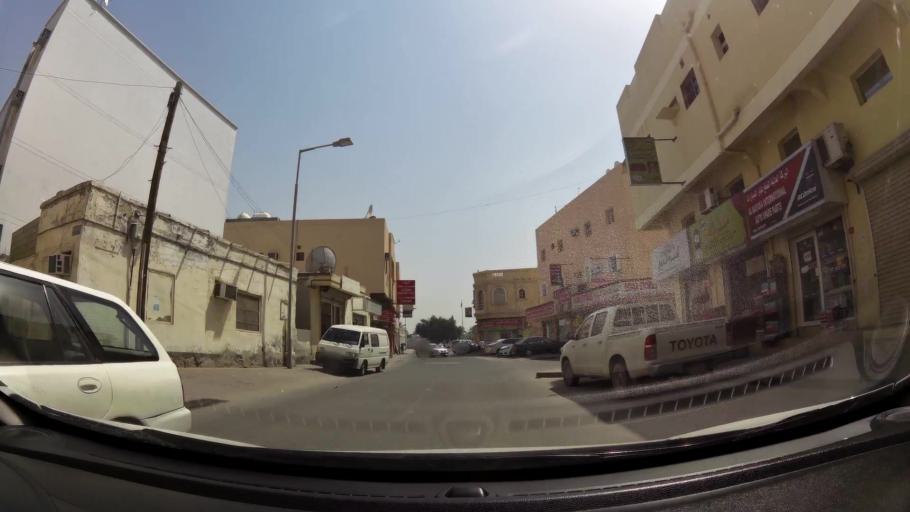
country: BH
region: Manama
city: Jidd Hafs
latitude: 26.2144
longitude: 50.4506
